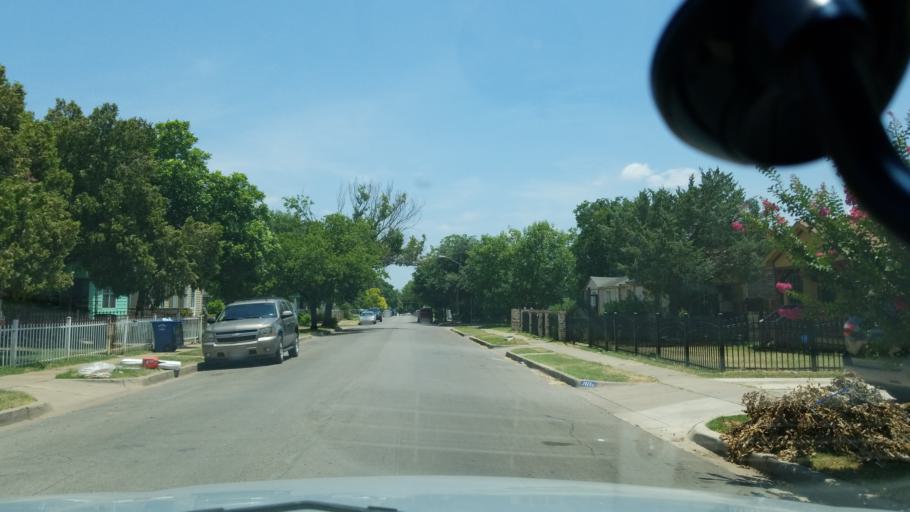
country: US
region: Texas
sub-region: Dallas County
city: Cockrell Hill
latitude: 32.7301
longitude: -96.8623
